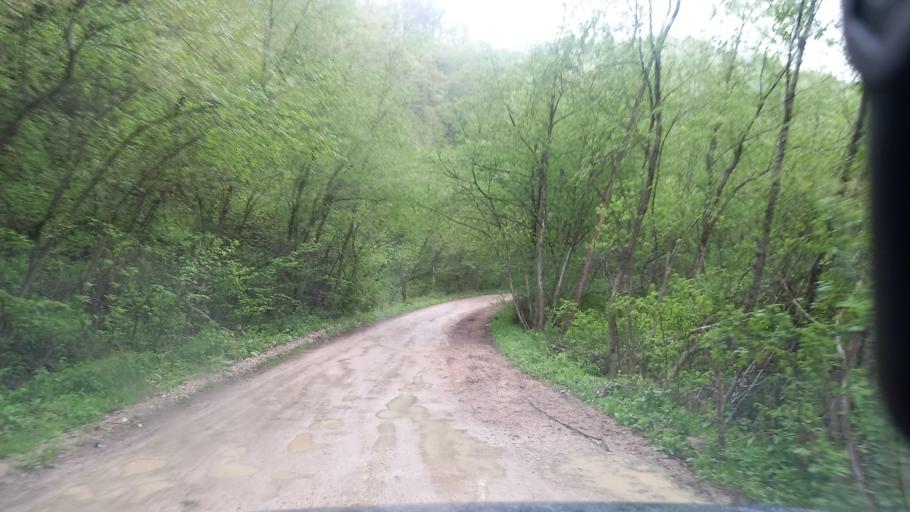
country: RU
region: Kabardino-Balkariya
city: Gundelen
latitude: 43.5798
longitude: 43.1082
